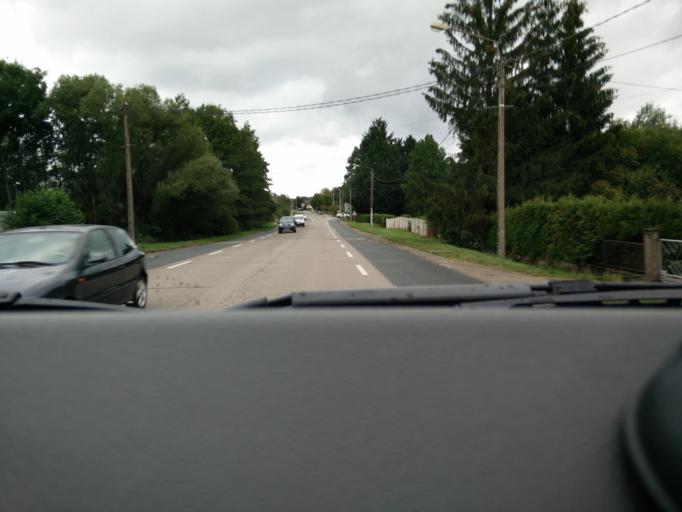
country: FR
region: Lorraine
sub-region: Departement des Vosges
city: Saint-Die-des-Vosges
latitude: 48.3078
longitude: 6.9239
